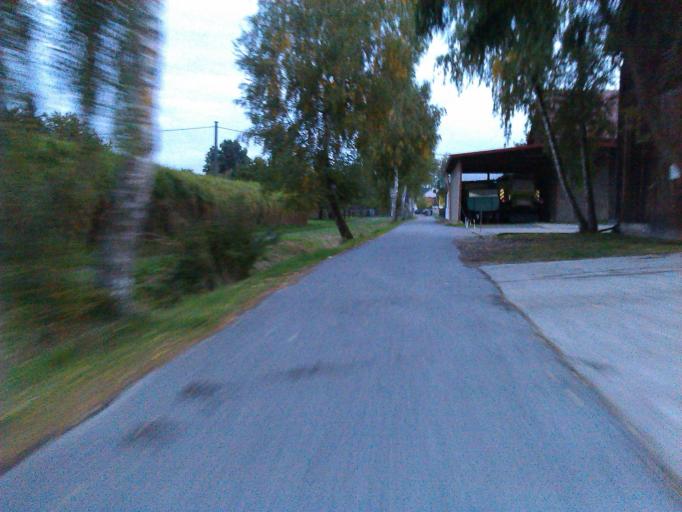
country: DE
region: Baden-Wuerttemberg
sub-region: Karlsruhe Region
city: Zuzenhausen
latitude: 49.2745
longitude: 8.8396
